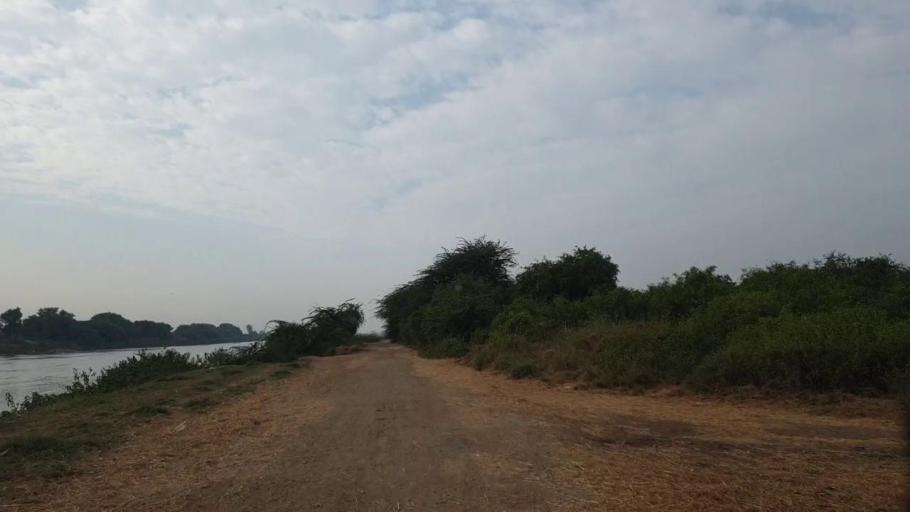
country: PK
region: Sindh
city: Tando Muhammad Khan
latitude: 25.0935
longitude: 68.4144
